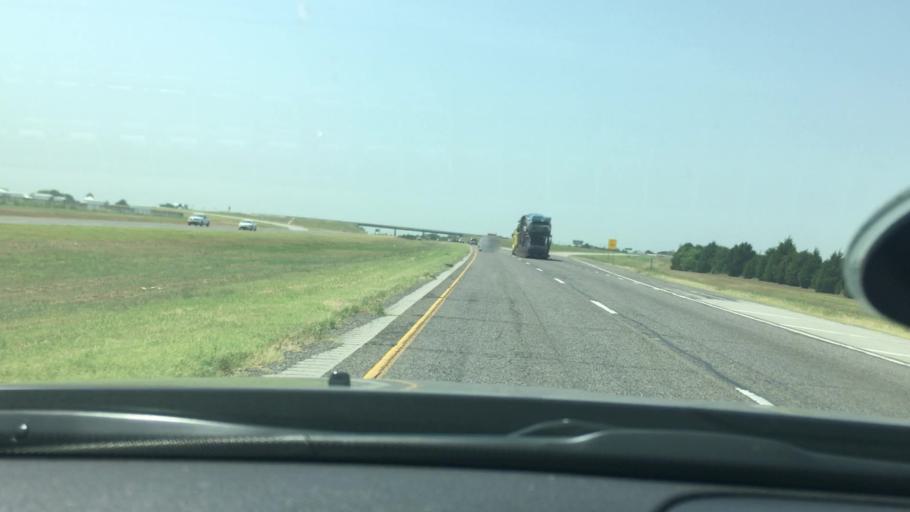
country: US
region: Oklahoma
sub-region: Garvin County
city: Wynnewood
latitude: 34.6280
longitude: -97.2173
